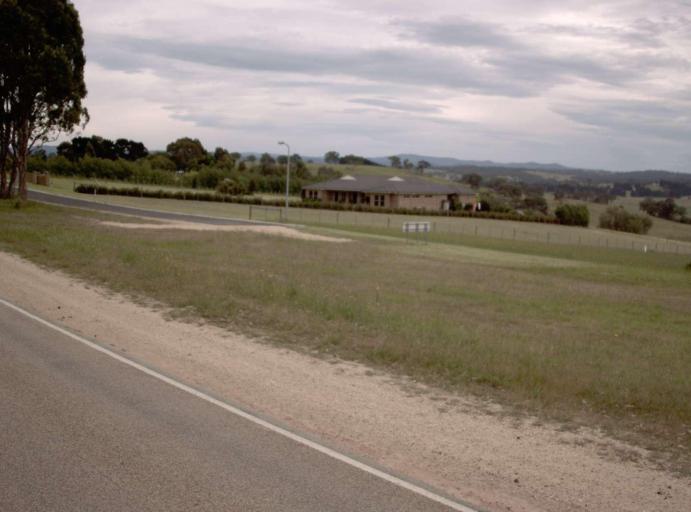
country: AU
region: Victoria
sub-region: East Gippsland
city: Bairnsdale
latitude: -37.7990
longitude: 147.6126
